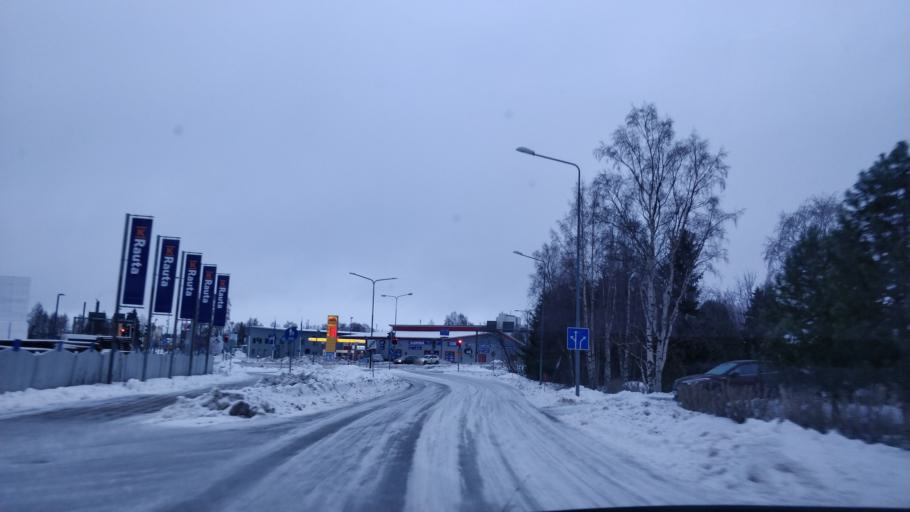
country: FI
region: Lapland
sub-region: Kemi-Tornio
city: Kemi
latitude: 65.7438
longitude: 24.5758
